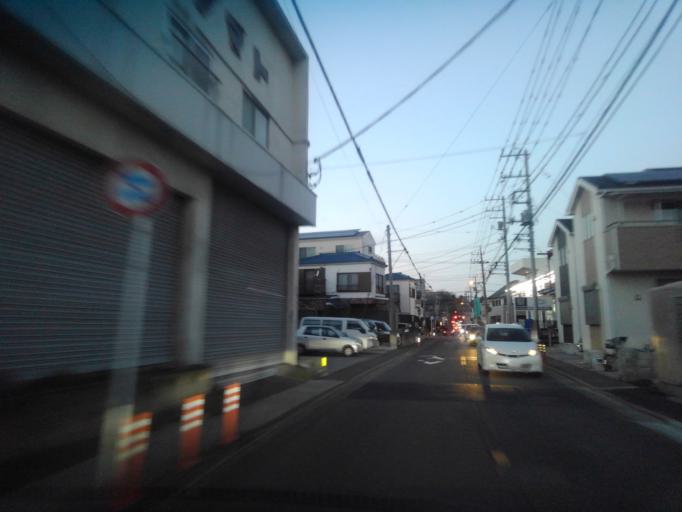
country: JP
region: Kanagawa
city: Minami-rinkan
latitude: 35.4992
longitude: 139.4647
